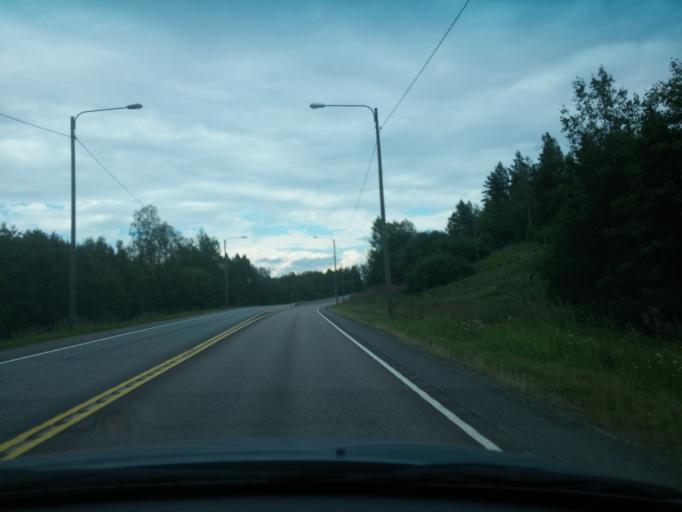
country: FI
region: Haeme
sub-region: Riihimaeki
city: Loppi
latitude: 60.7314
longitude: 24.5321
